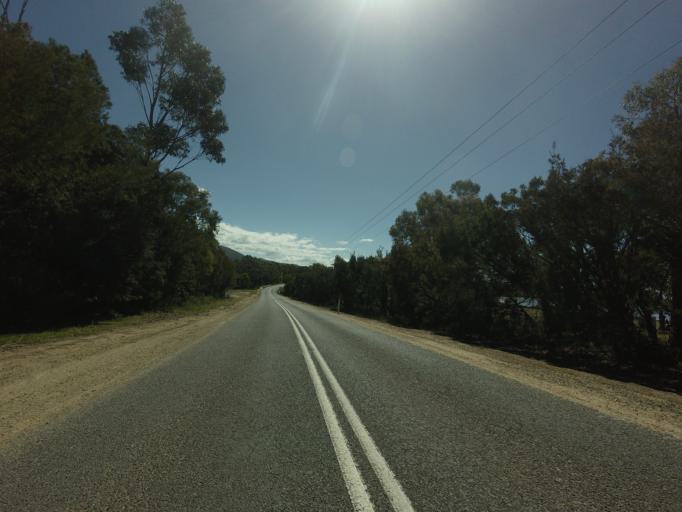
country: AU
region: Tasmania
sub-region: Break O'Day
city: St Helens
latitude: -41.8373
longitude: 148.2552
